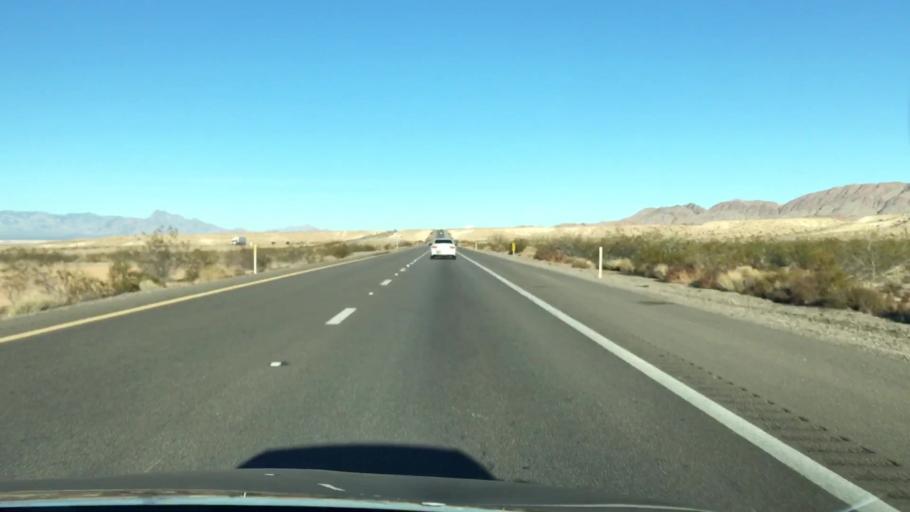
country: US
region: Nevada
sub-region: Clark County
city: Moapa Town
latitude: 36.5610
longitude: -114.6836
